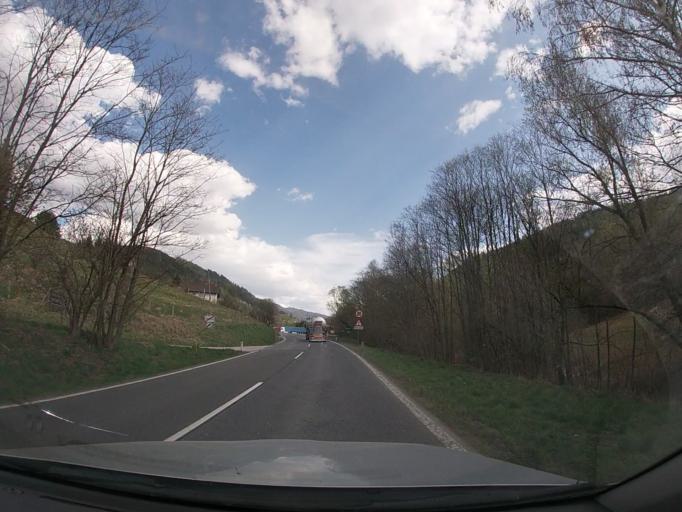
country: AT
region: Styria
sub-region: Politischer Bezirk Murau
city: Sankt Lorenzen bei Scheifling
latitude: 47.1407
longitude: 14.4228
